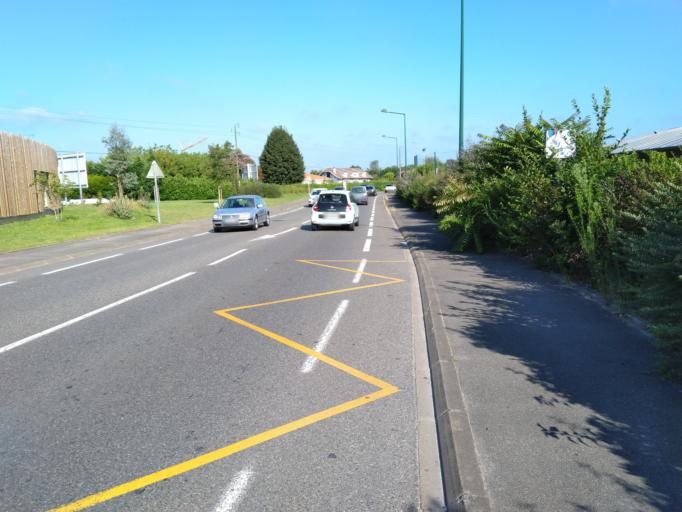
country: FR
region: Aquitaine
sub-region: Departement des Landes
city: Saint-Paul-les-Dax
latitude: 43.7372
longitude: -1.0514
